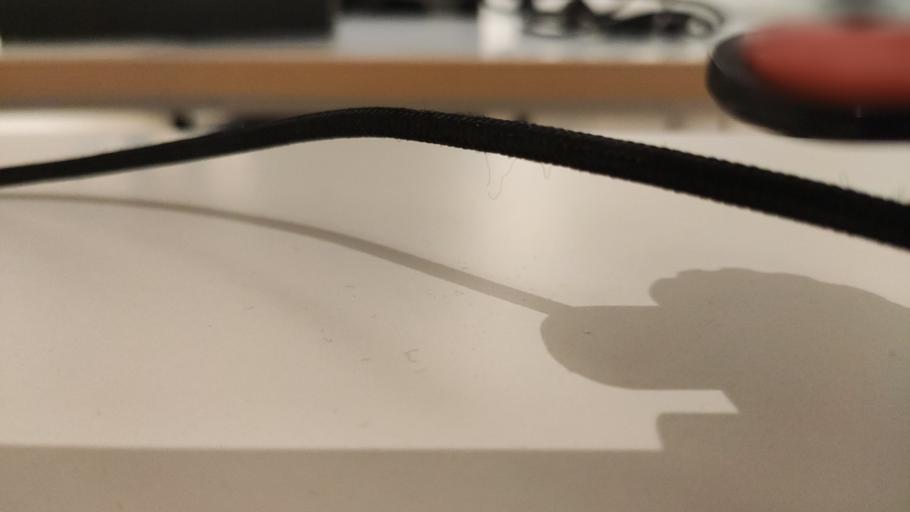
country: RU
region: Moskovskaya
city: Dorokhovo
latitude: 55.3868
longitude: 36.3954
